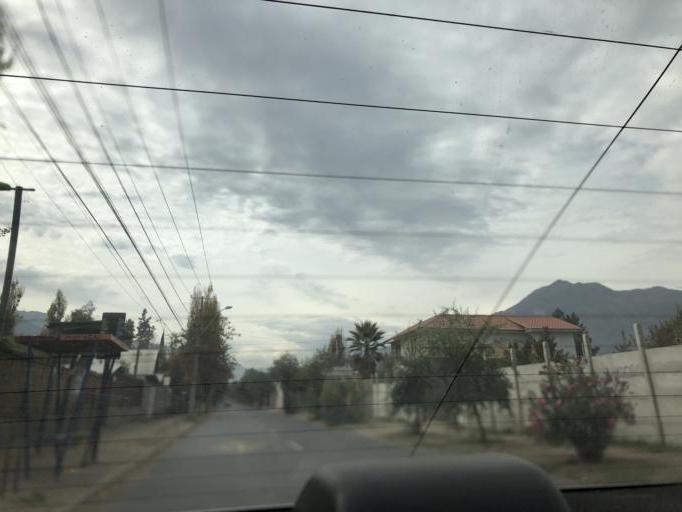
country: CL
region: Santiago Metropolitan
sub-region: Provincia de Cordillera
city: Puente Alto
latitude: -33.6069
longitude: -70.5199
